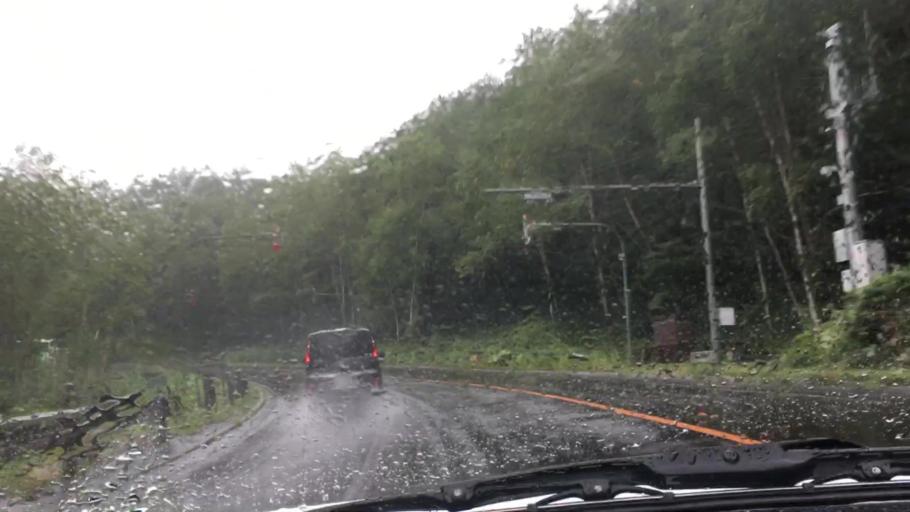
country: JP
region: Hokkaido
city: Sapporo
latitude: 42.8837
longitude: 141.1401
